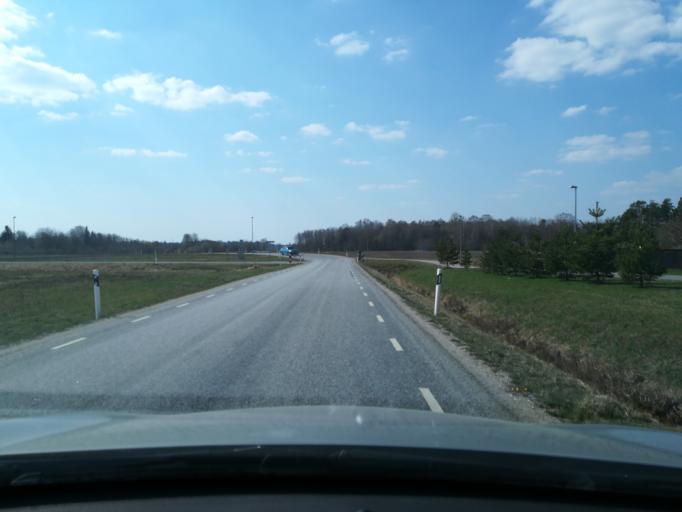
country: EE
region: Harju
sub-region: Saue vald
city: Laagri
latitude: 59.3414
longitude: 24.5888
